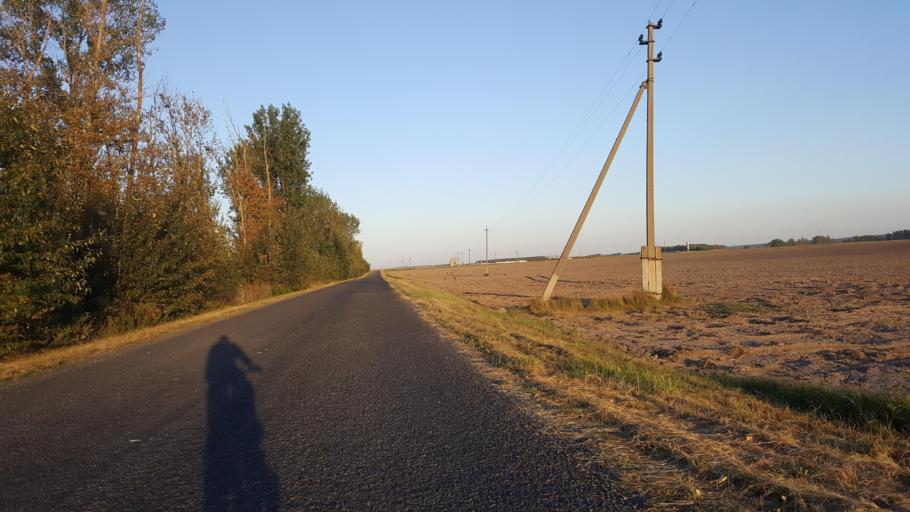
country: BY
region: Brest
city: Vysokaye
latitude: 52.2968
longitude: 23.5259
